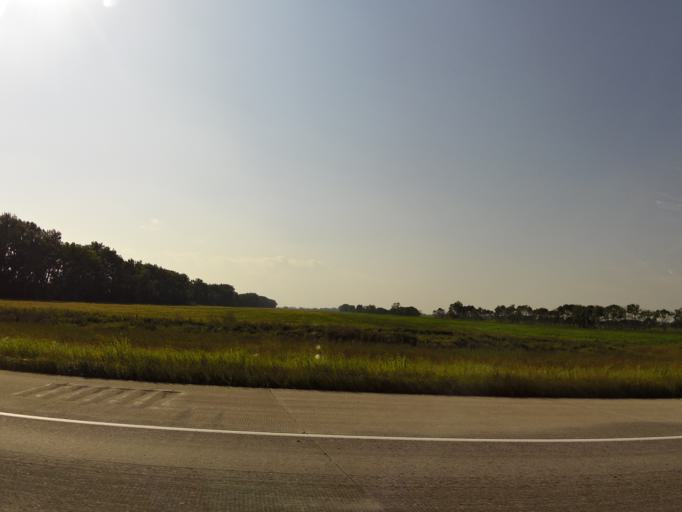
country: US
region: North Dakota
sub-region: Grand Forks County
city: Grand Forks
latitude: 48.1184
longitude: -97.1918
